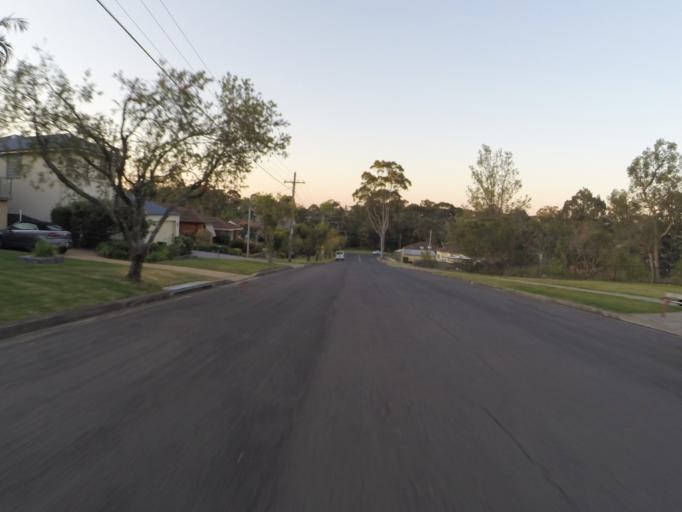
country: AU
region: New South Wales
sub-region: Bankstown
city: Revesby
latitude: -33.9663
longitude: 151.0126
